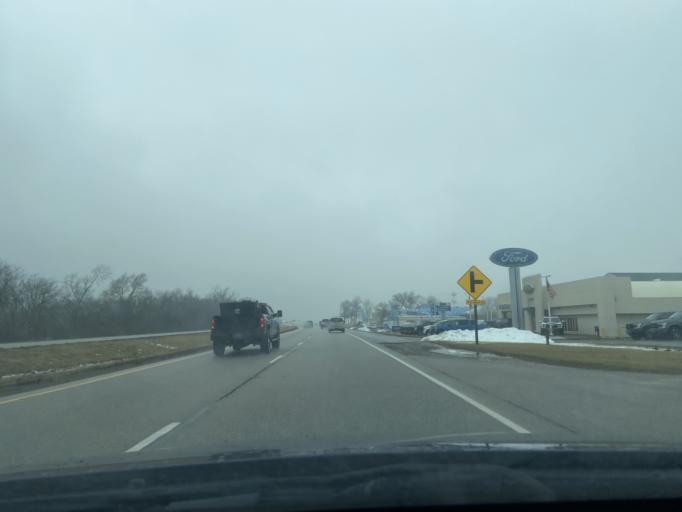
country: US
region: Illinois
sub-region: Lake County
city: Wauconda
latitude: 42.2812
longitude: -88.1552
